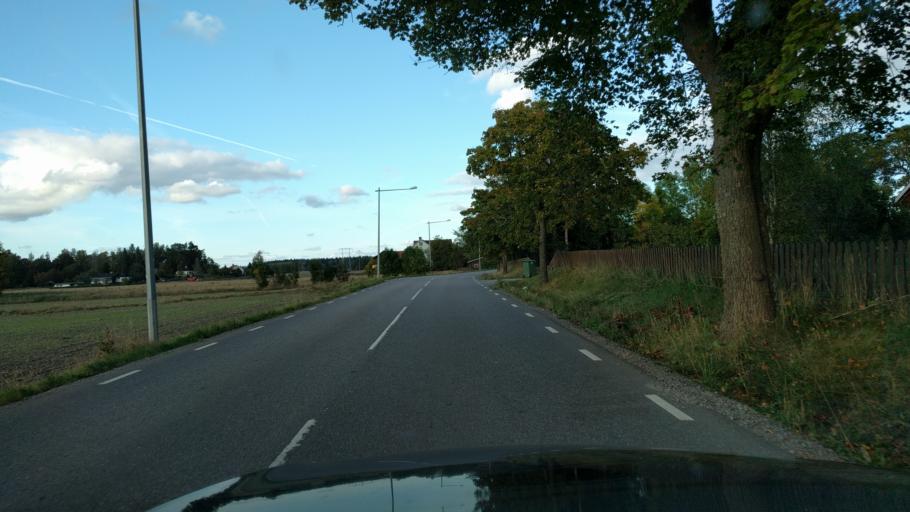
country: SE
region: Uppsala
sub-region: Osthammars Kommun
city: Bjorklinge
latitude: 60.1539
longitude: 17.5897
